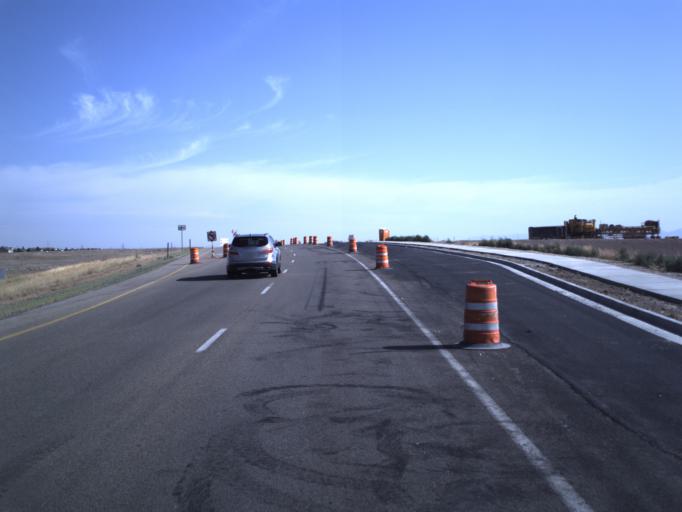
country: US
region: Utah
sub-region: Salt Lake County
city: Herriman
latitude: 40.5101
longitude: -112.0037
